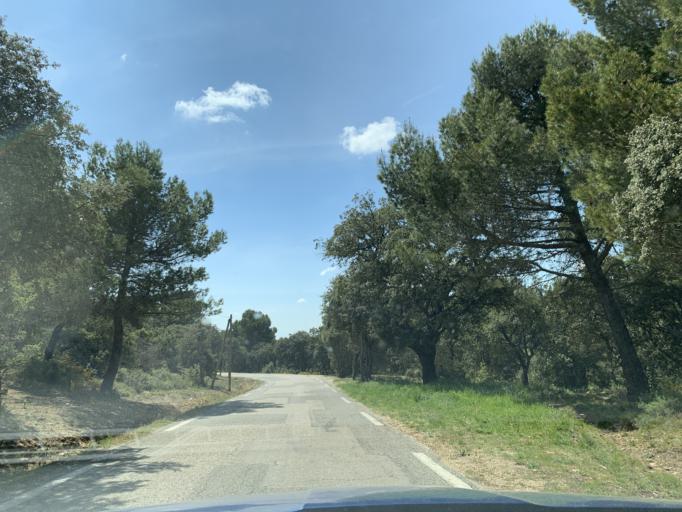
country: FR
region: Provence-Alpes-Cote d'Azur
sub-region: Departement du Vaucluse
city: Saint-Didier
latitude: 43.9632
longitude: 5.1105
